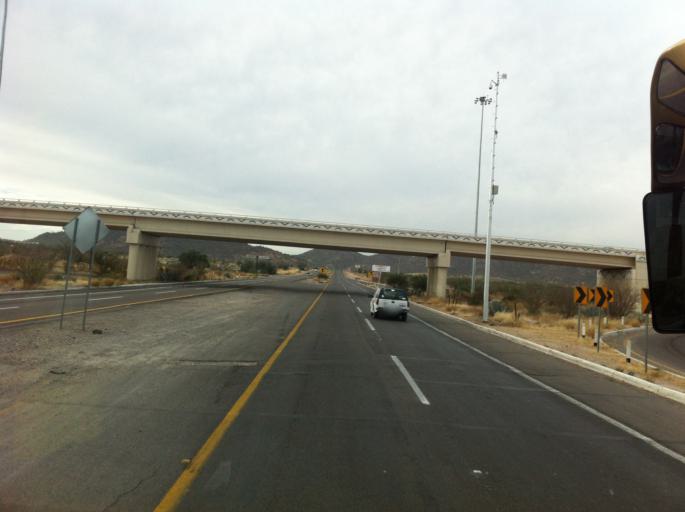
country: MX
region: Sonora
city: Hermosillo
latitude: 29.0104
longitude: -110.9637
